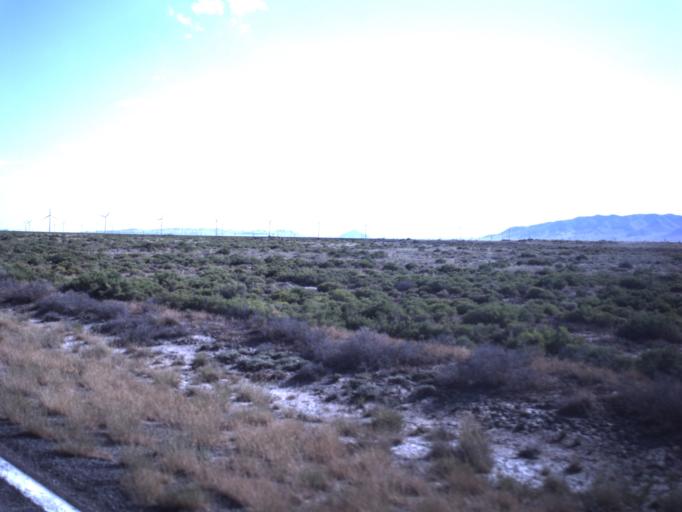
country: US
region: Utah
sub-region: Beaver County
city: Milford
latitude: 38.5222
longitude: -112.9912
